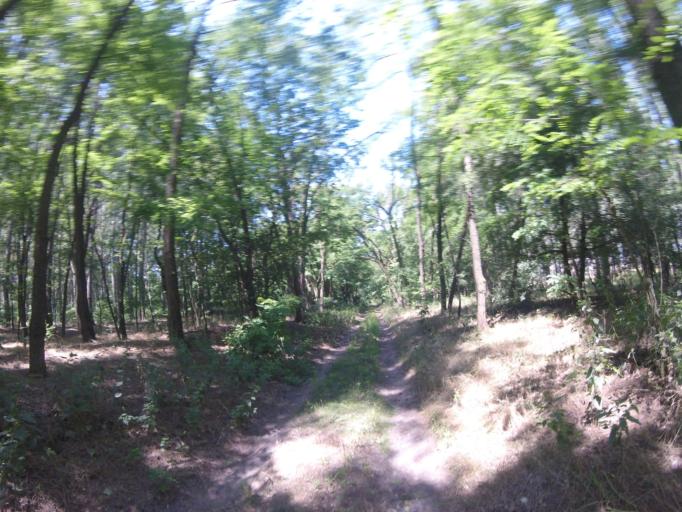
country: HU
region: Pest
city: Nagykoros
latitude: 47.0703
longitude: 19.7545
